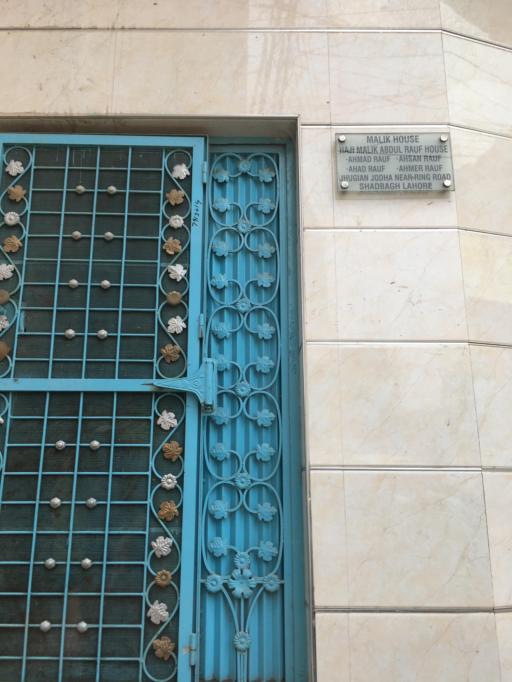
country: PK
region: Punjab
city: Lahore
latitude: 31.6183
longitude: 74.3459
